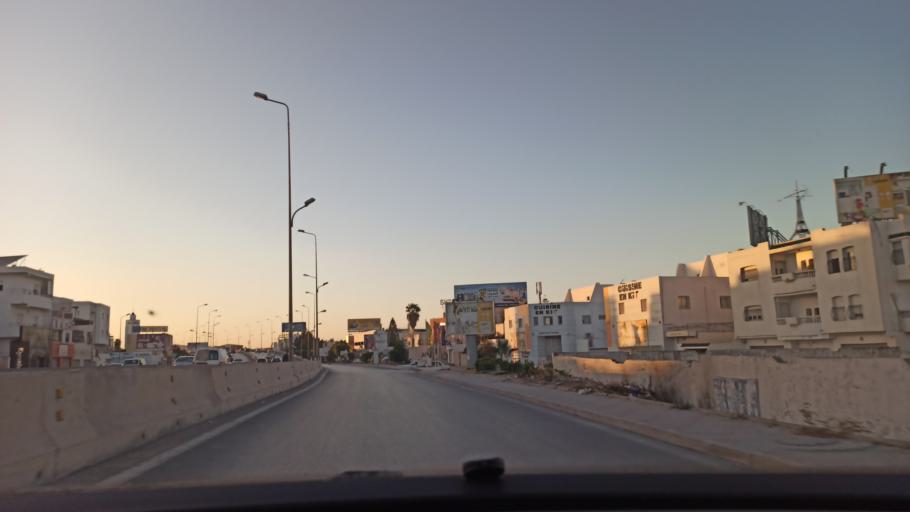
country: TN
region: Ariana
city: Ariana
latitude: 36.8618
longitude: 10.2023
